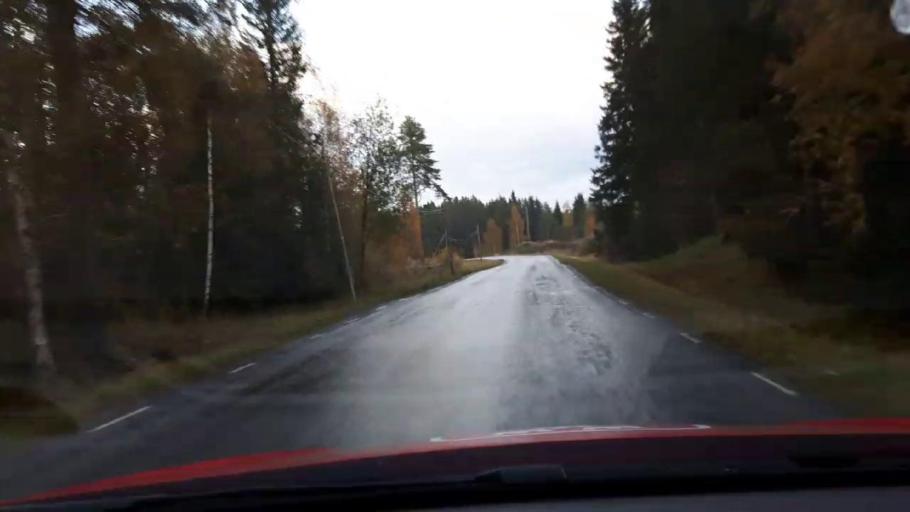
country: SE
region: Jaemtland
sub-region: OEstersunds Kommun
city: Lit
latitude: 63.3252
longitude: 14.8804
